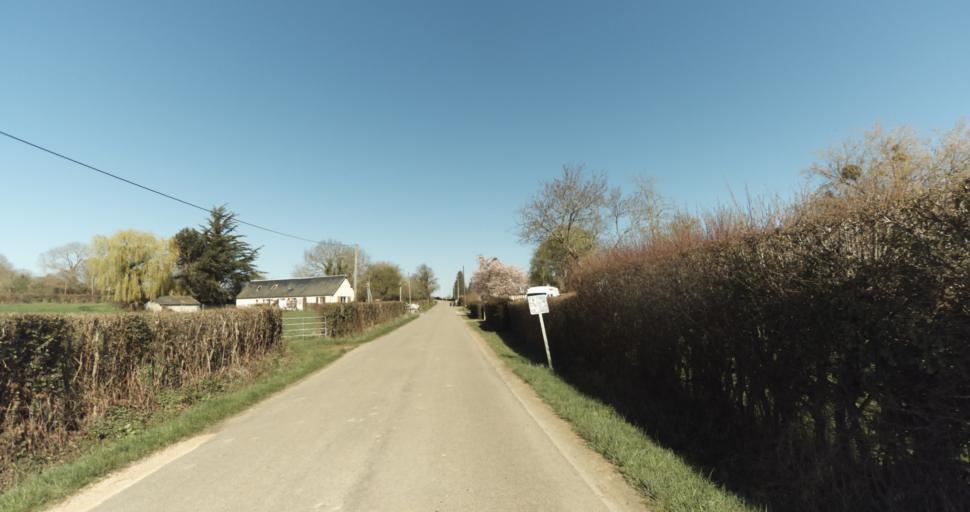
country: FR
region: Lower Normandy
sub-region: Departement du Calvados
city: Saint-Pierre-sur-Dives
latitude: 48.9879
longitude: 0.0289
